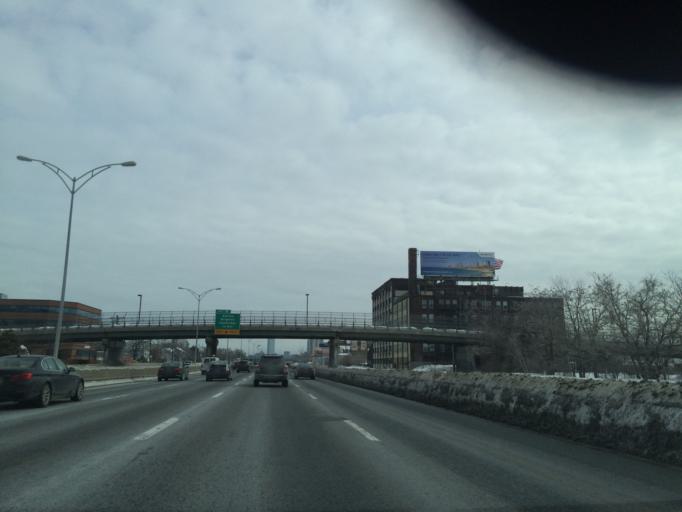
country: US
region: Massachusetts
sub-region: Norfolk County
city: Brookline
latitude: 42.3575
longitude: -71.1396
